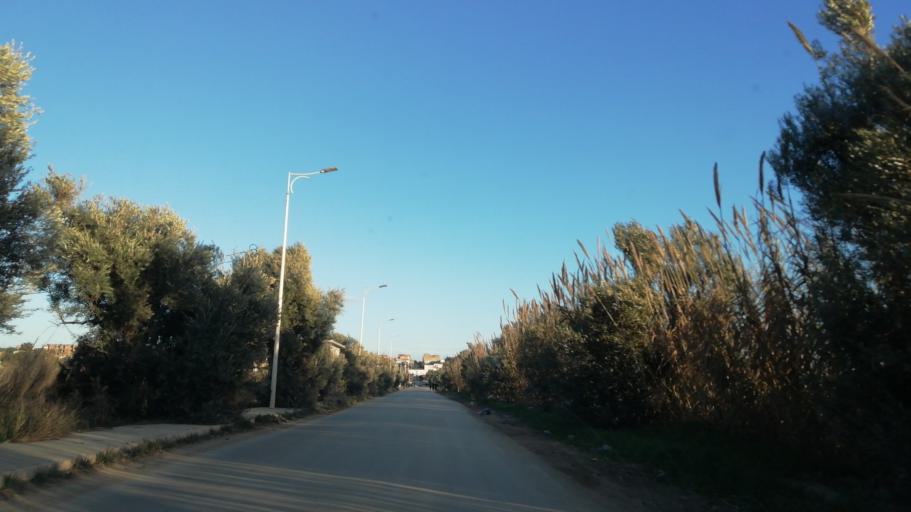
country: DZ
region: Oran
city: Sidi ech Chahmi
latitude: 35.6944
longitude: -0.5094
